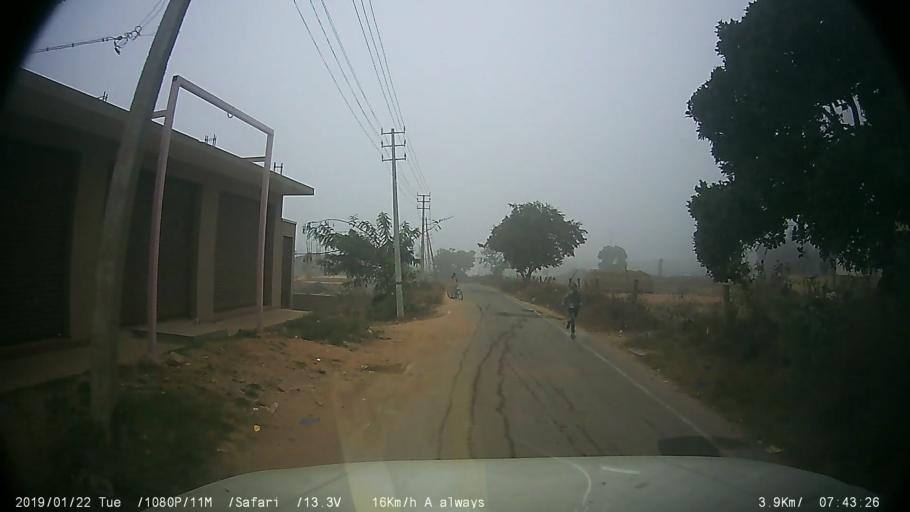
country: IN
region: Karnataka
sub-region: Bangalore Urban
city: Anekal
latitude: 12.8257
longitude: 77.6305
